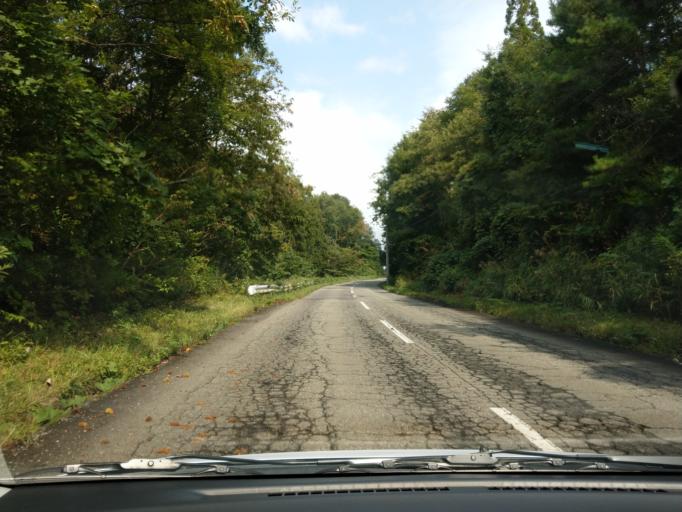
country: JP
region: Akita
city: Omagari
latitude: 39.4835
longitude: 140.3119
